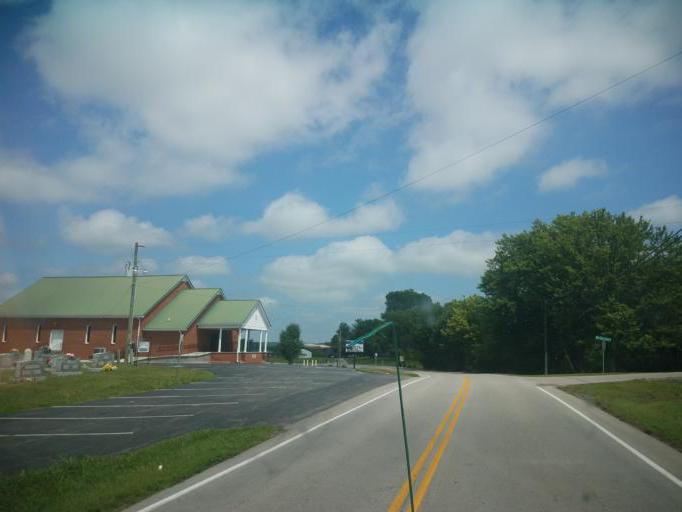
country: US
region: Kentucky
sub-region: Barren County
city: Glasgow
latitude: 36.9181
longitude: -85.7867
